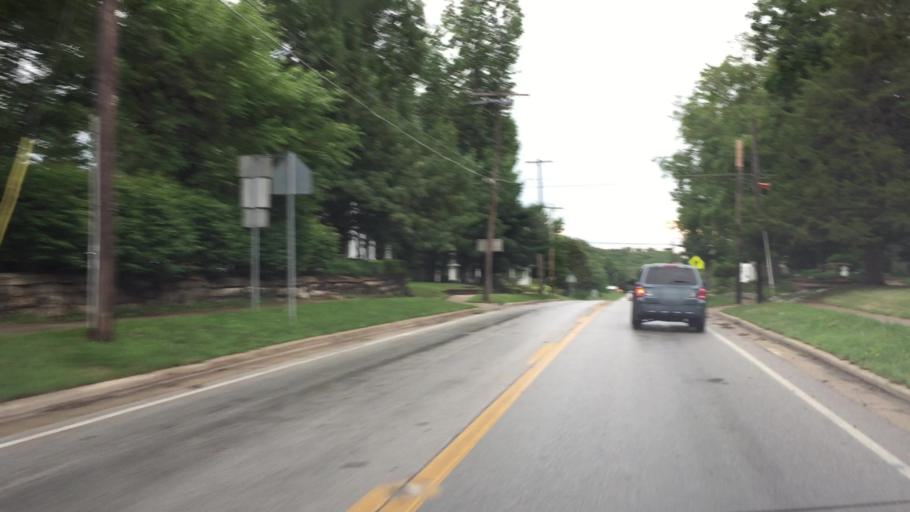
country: US
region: Illinois
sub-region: Hancock County
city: Hamilton
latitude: 40.3929
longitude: -91.3398
